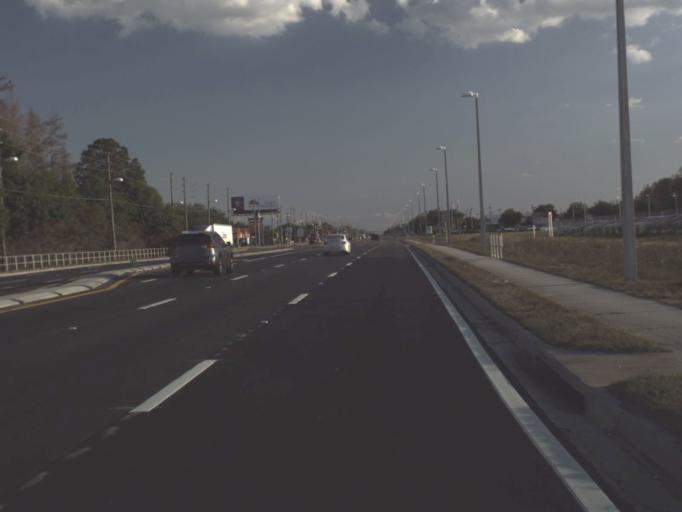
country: US
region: Florida
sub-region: Orange County
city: Southchase
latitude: 28.4186
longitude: -81.4048
